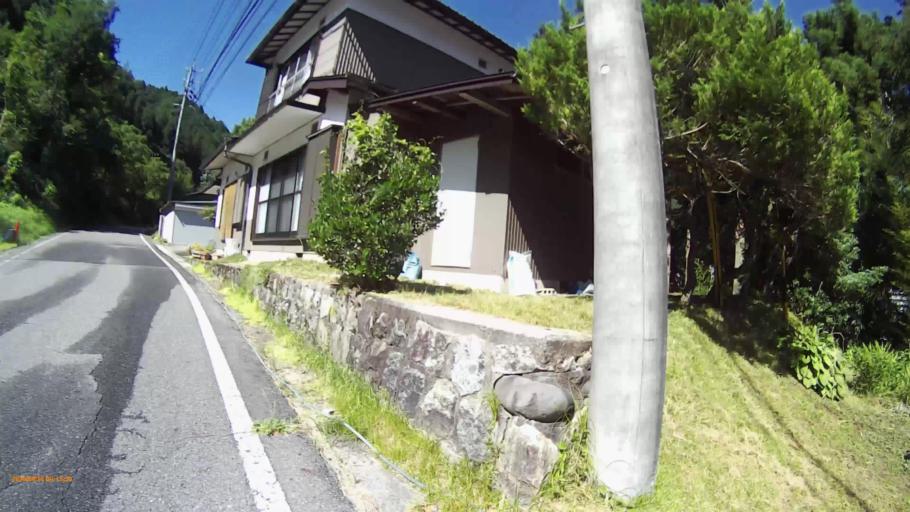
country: JP
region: Nagano
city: Iida
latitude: 35.6952
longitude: 137.6843
